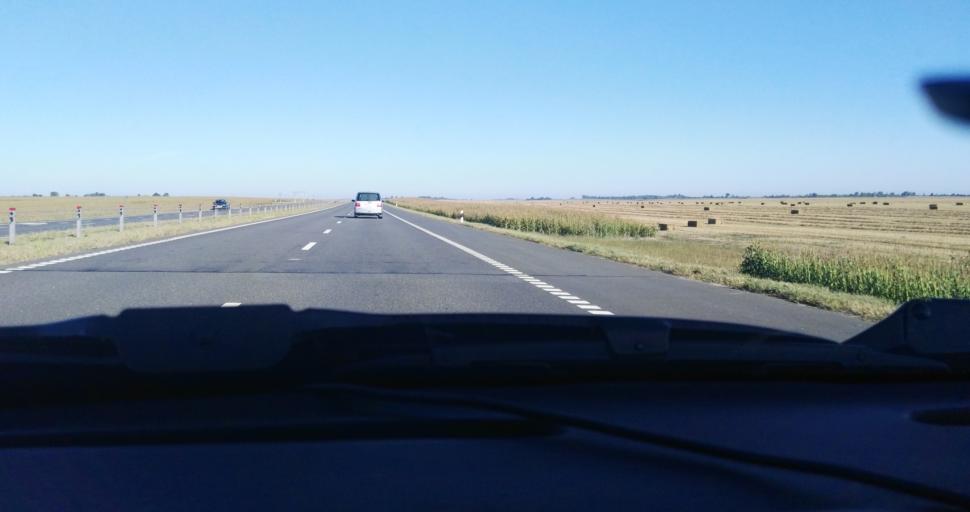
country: BY
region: Gomel
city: Buda-Kashalyova
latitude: 52.5228
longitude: 30.6226
